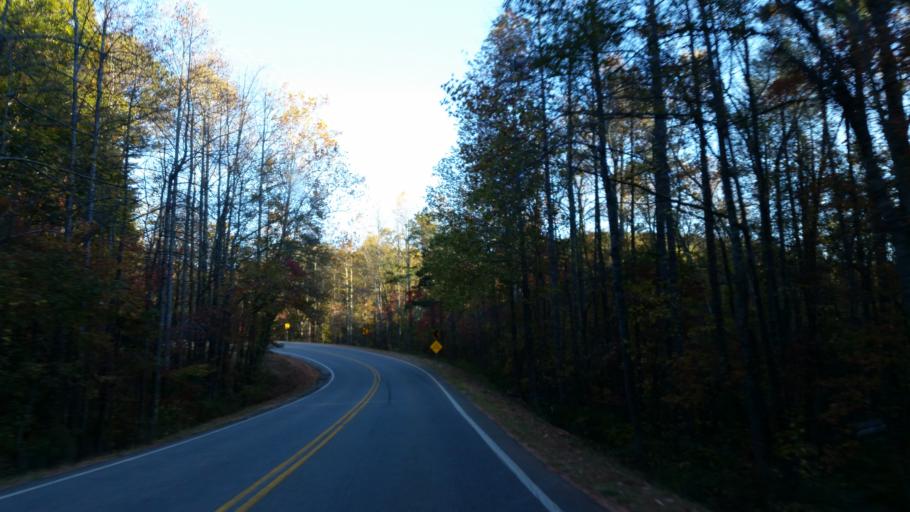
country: US
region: Georgia
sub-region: Dawson County
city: Dawsonville
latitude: 34.5508
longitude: -84.2424
